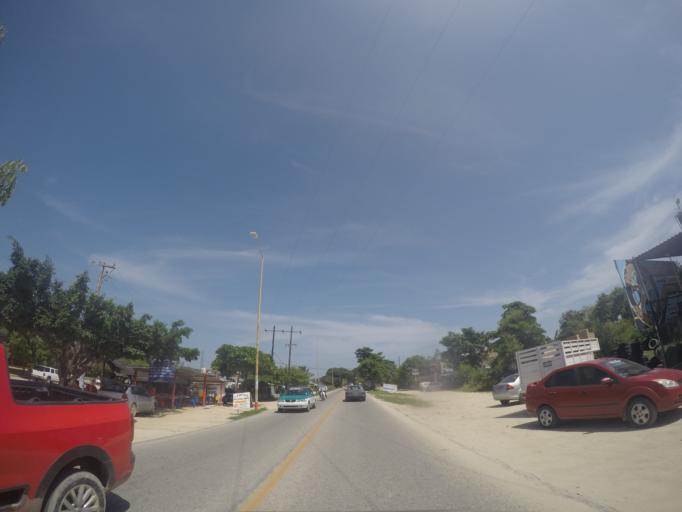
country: MX
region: Oaxaca
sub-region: Villa de Tututepec de Melchor Ocampo
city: Santa Rosa de Lima
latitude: 16.0094
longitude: -97.4348
